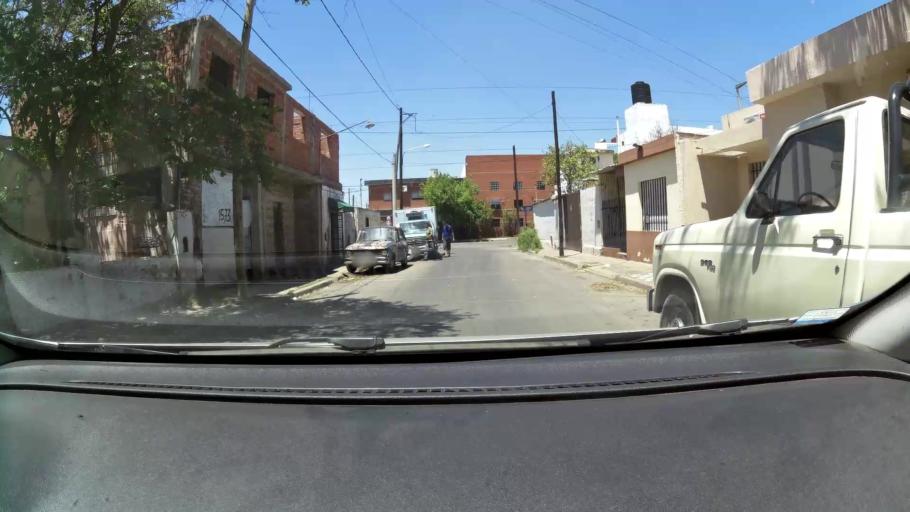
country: AR
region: Cordoba
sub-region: Departamento de Capital
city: Cordoba
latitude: -31.4273
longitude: -64.1255
